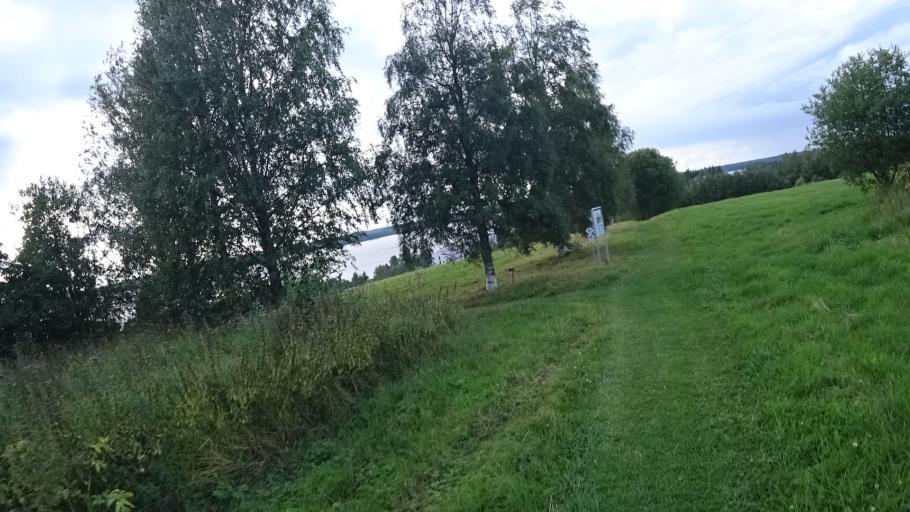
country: FI
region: North Karelia
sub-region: Joensuu
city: Ilomantsi
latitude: 62.6728
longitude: 30.9181
